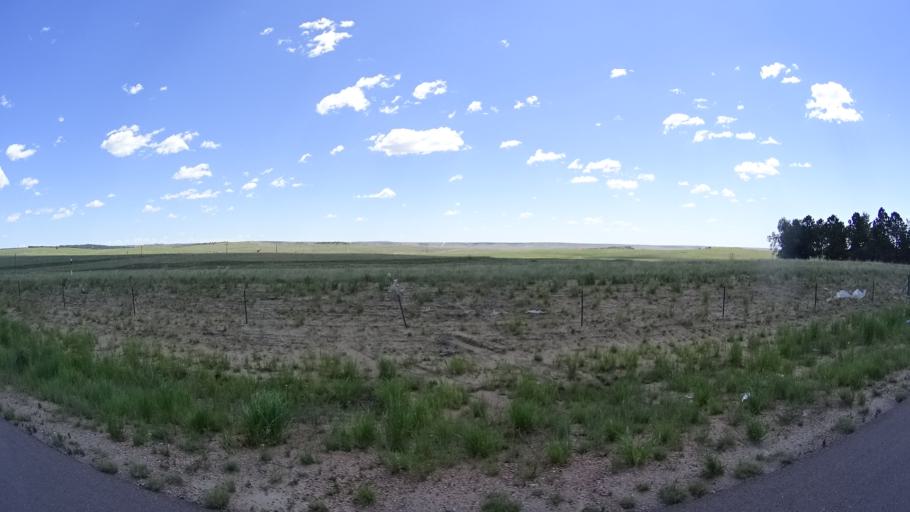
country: US
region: Colorado
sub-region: El Paso County
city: Cimarron Hills
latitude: 38.8355
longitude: -104.6827
